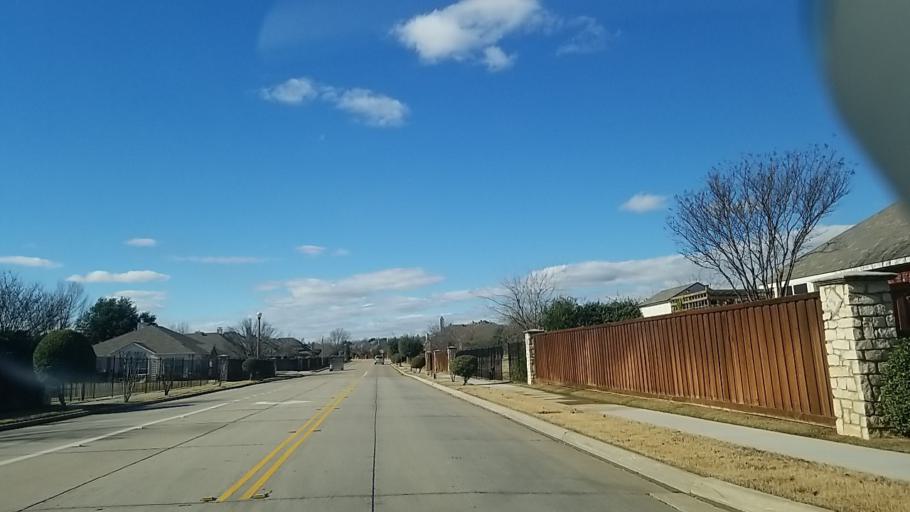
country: US
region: Texas
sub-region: Denton County
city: Corinth
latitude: 33.1769
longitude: -97.1040
